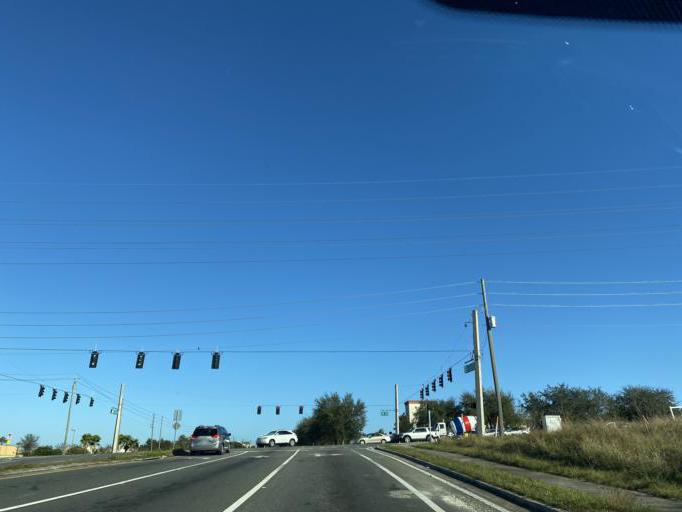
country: US
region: Florida
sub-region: Lake County
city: Minneola
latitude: 28.5461
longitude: -81.7232
